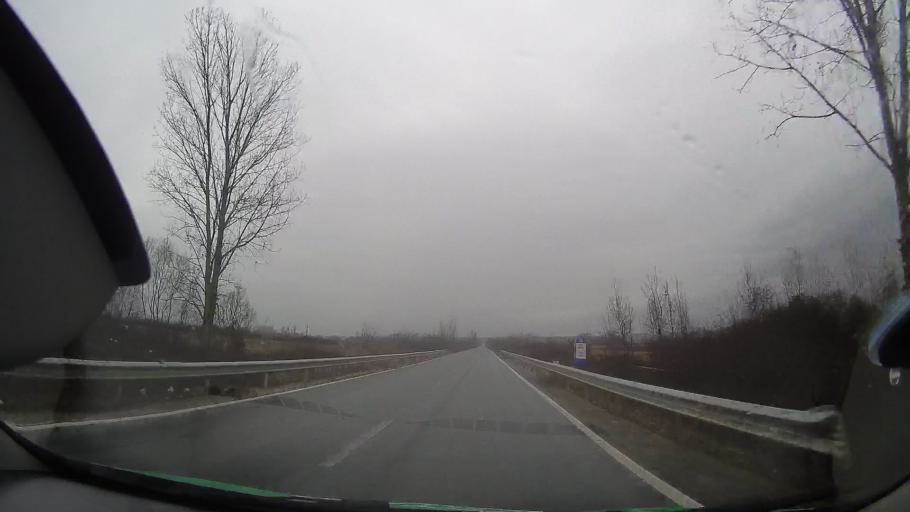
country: RO
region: Bihor
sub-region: Comuna Tinca
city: Tinca
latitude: 46.7490
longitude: 21.9380
